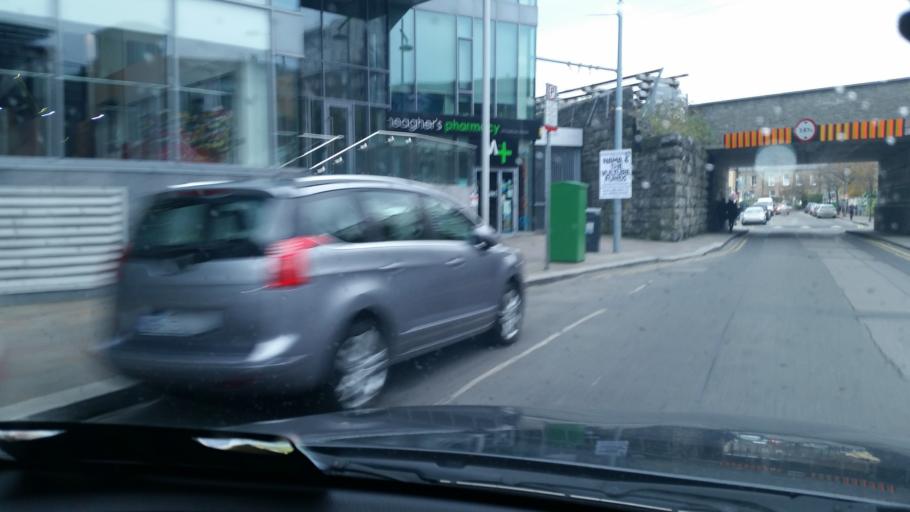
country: IE
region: Leinster
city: Ringsend
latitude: 53.3395
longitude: -6.2366
